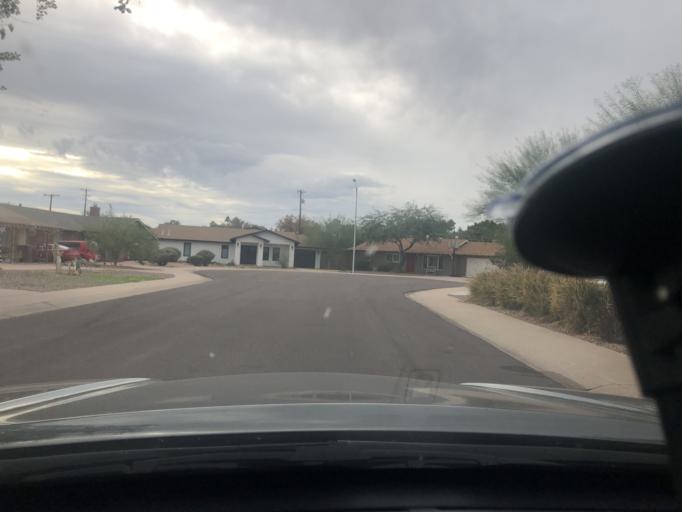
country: US
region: Arizona
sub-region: Maricopa County
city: Scottsdale
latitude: 33.4827
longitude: -111.9004
